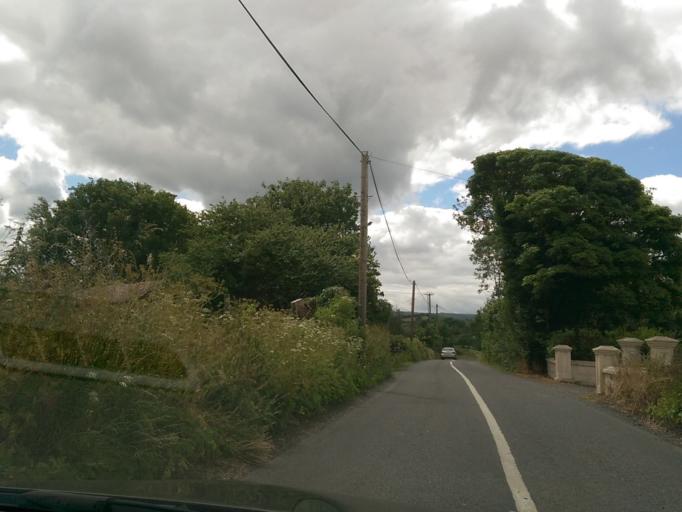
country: IE
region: Munster
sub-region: North Tipperary
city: Nenagh
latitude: 52.8350
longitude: -8.2028
